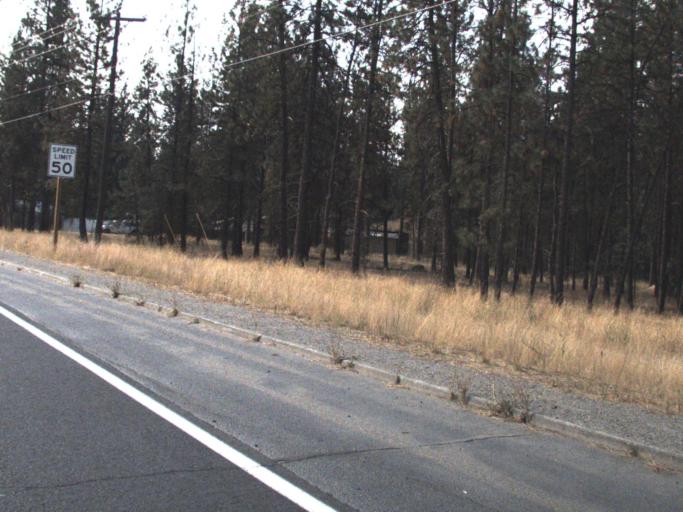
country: US
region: Washington
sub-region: Spokane County
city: Town and Country
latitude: 47.7357
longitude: -117.5075
